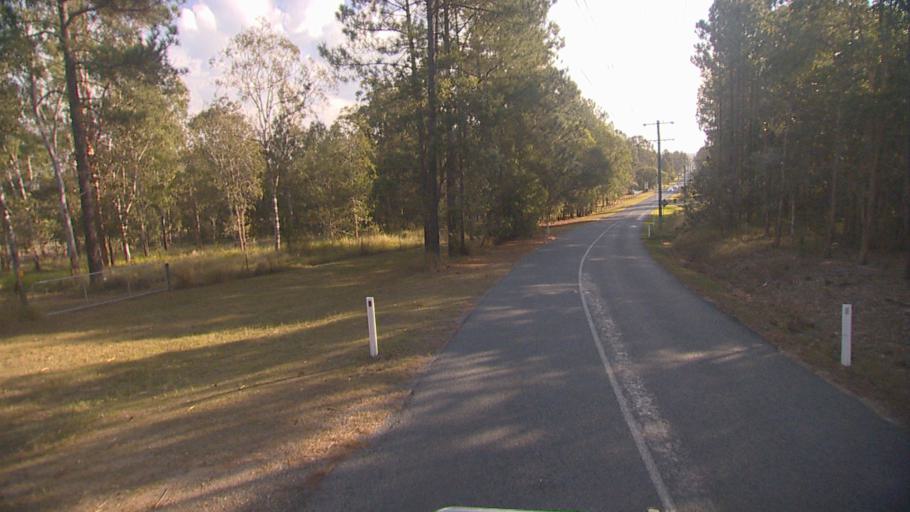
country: AU
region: Queensland
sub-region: Logan
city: Cedar Vale
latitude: -27.8499
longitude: 153.1202
